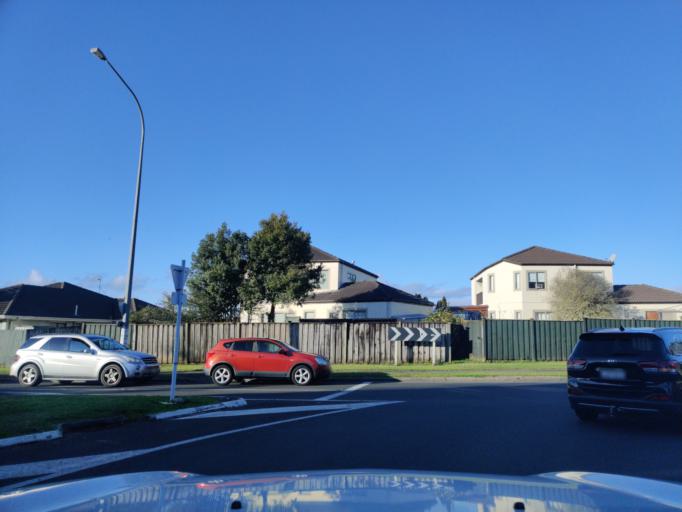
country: NZ
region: Auckland
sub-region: Auckland
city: Pakuranga
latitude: -36.9144
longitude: 174.9081
